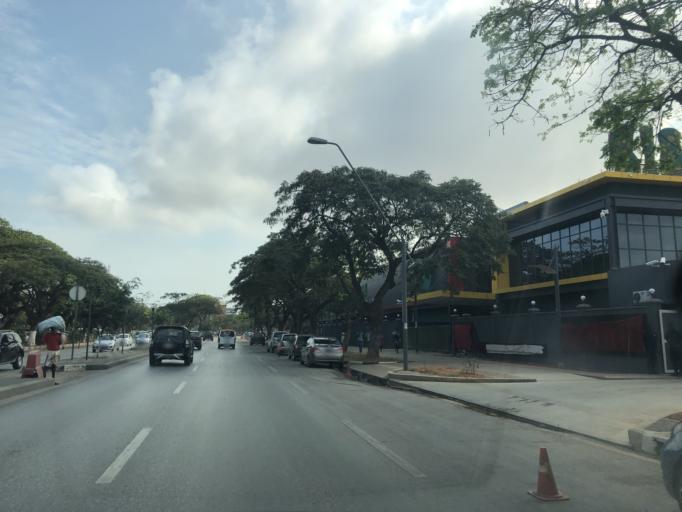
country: AO
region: Luanda
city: Luanda
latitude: -8.8355
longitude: 13.2380
